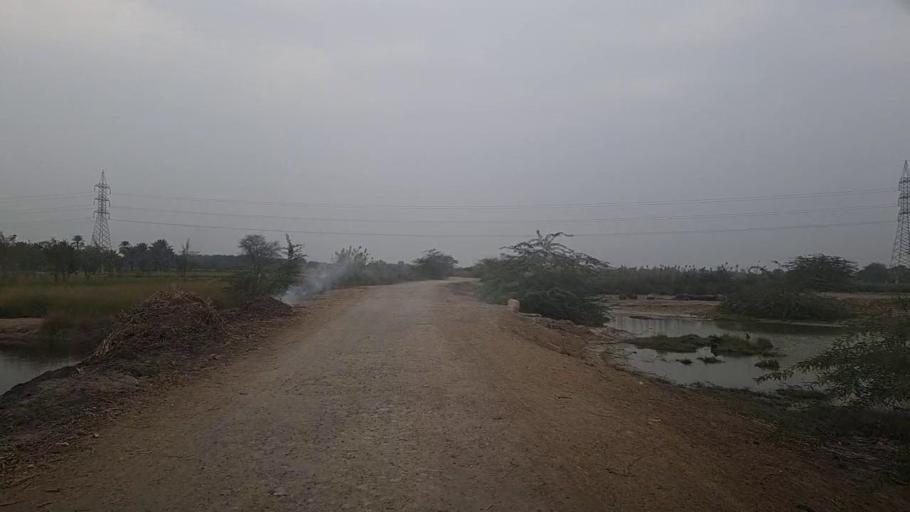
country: PK
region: Sindh
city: Gambat
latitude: 27.3415
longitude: 68.6017
